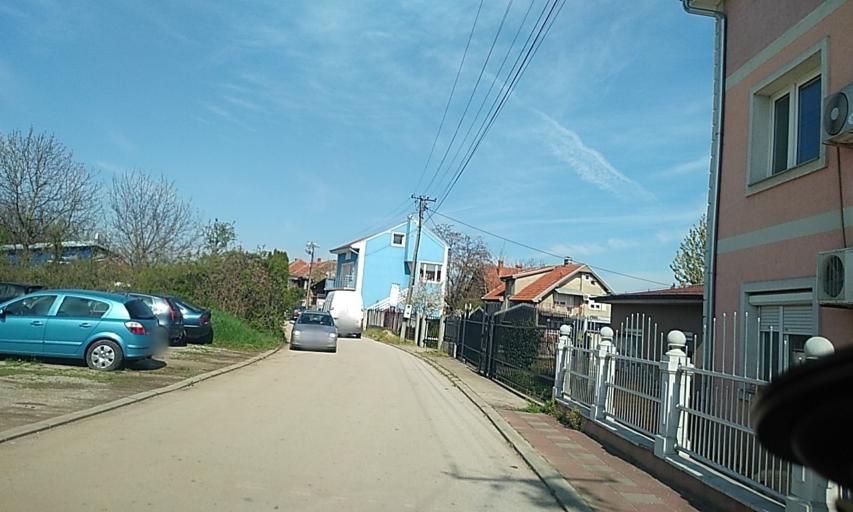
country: RS
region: Central Serbia
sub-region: Nisavski Okrug
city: Niska Banja
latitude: 43.3075
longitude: 21.9688
